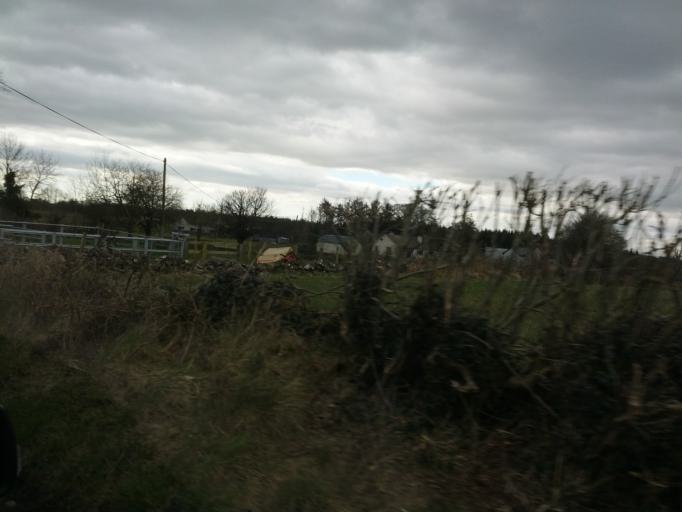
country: IE
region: Connaught
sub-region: County Galway
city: Athenry
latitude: 53.3721
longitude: -8.6406
